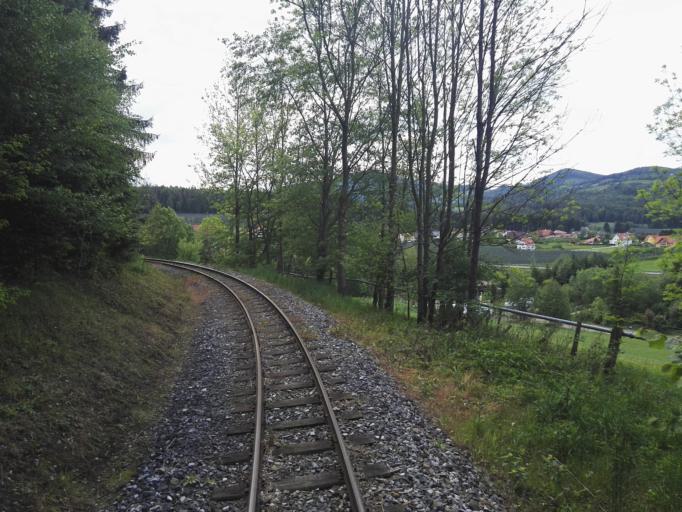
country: AT
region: Styria
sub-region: Politischer Bezirk Weiz
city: Baierdorf-Umgebung
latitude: 47.2560
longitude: 15.7164
